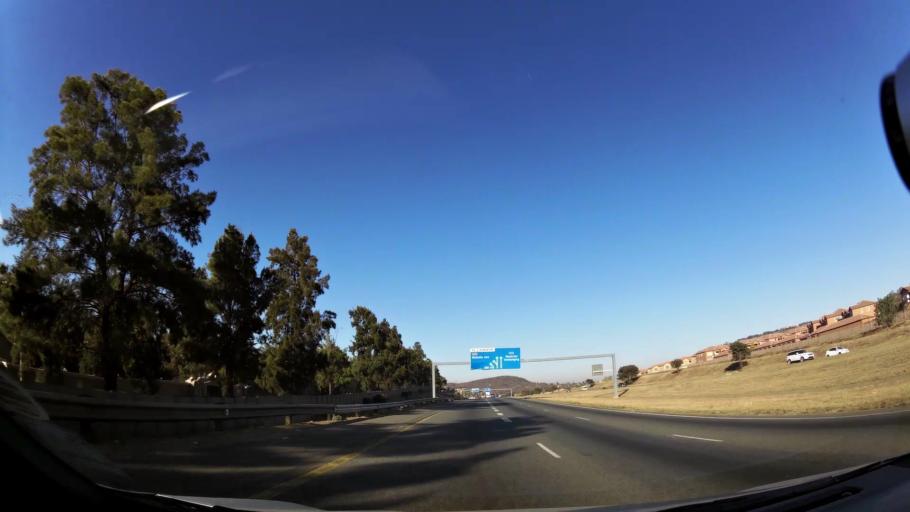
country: ZA
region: Gauteng
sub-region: Ekurhuleni Metropolitan Municipality
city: Germiston
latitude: -26.2793
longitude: 28.1037
